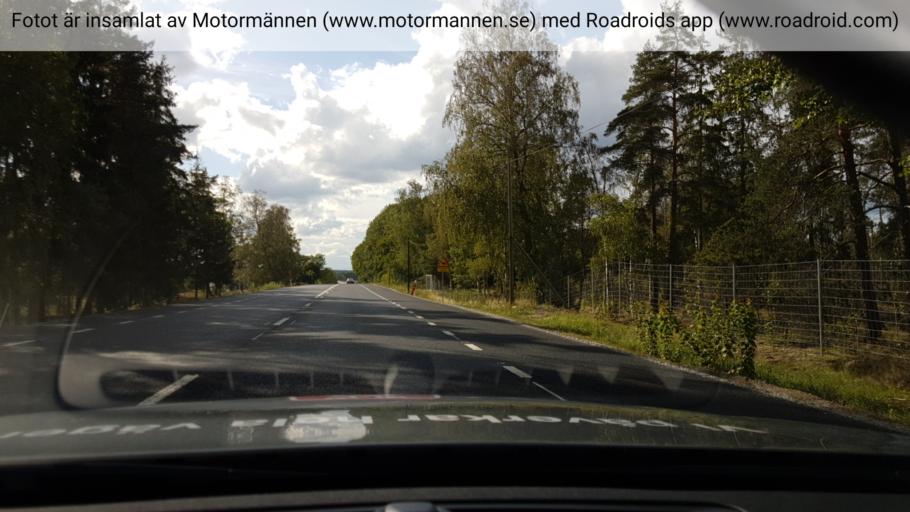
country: SE
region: Uppsala
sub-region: Enkopings Kommun
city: Grillby
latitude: 59.6614
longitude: 17.2825
